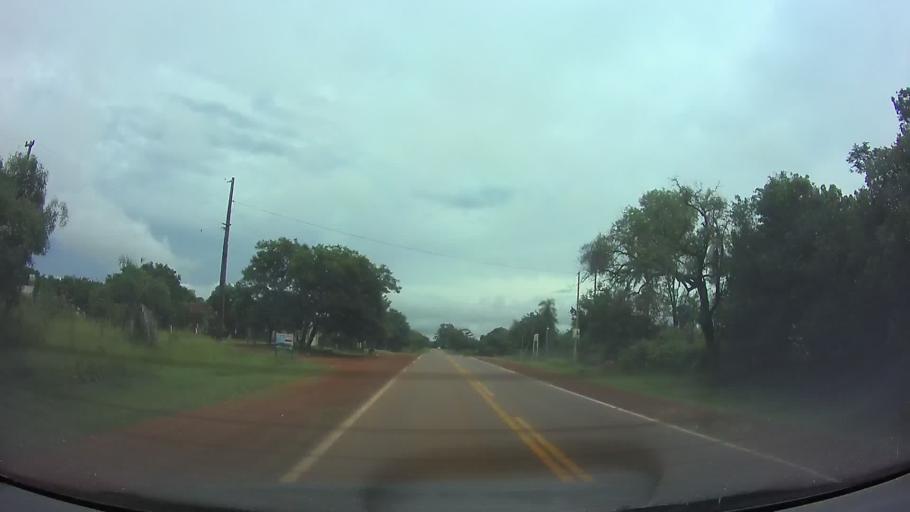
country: PY
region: Paraguari
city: Acahay
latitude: -25.8705
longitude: -57.1260
